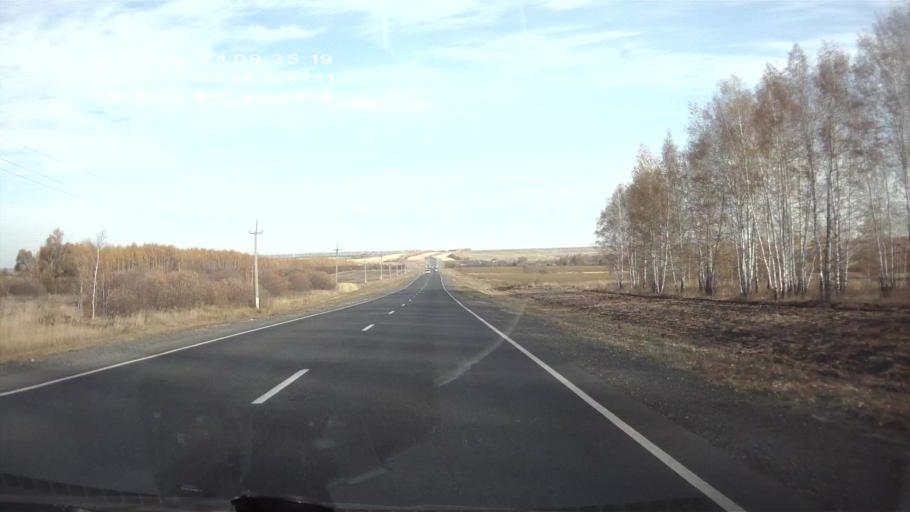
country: RU
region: Penza
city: Mokshan
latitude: 53.6019
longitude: 44.7263
